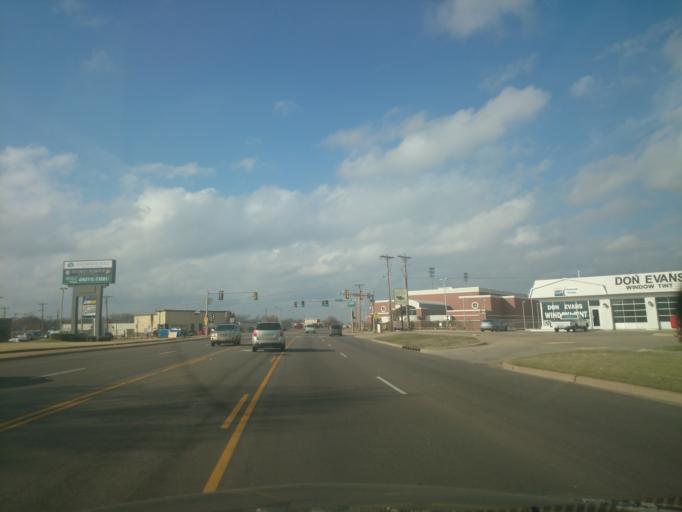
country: US
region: Oklahoma
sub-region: Payne County
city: Stillwater
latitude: 36.1336
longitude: -97.0620
